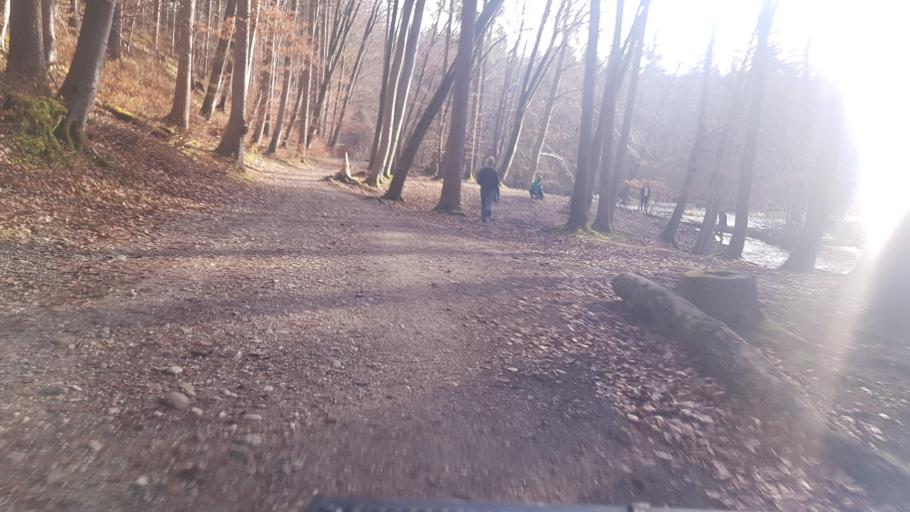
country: DE
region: Bavaria
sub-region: Upper Bavaria
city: Gauting
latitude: 48.0421
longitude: 11.3721
